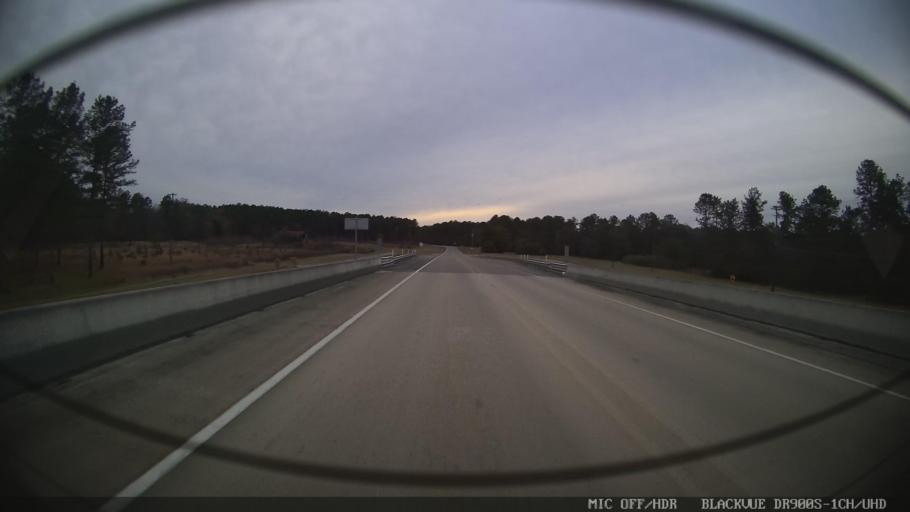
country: US
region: Mississippi
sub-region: Clarke County
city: Quitman
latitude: 32.0424
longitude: -88.7453
